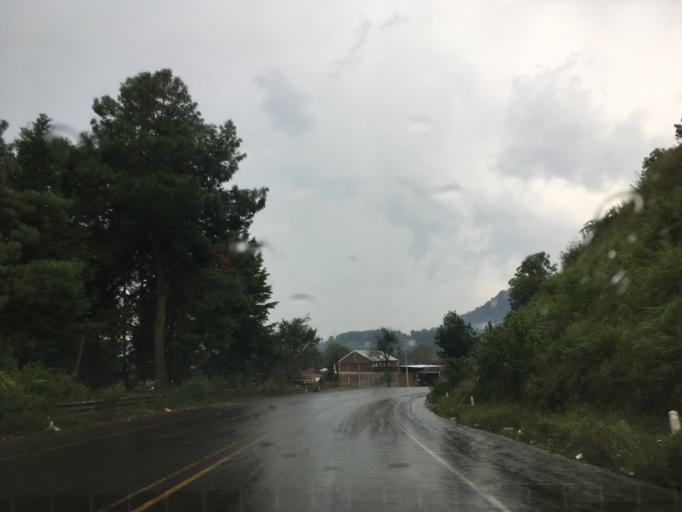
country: MX
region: Michoacan
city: Angahuan
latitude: 19.5544
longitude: -102.2205
